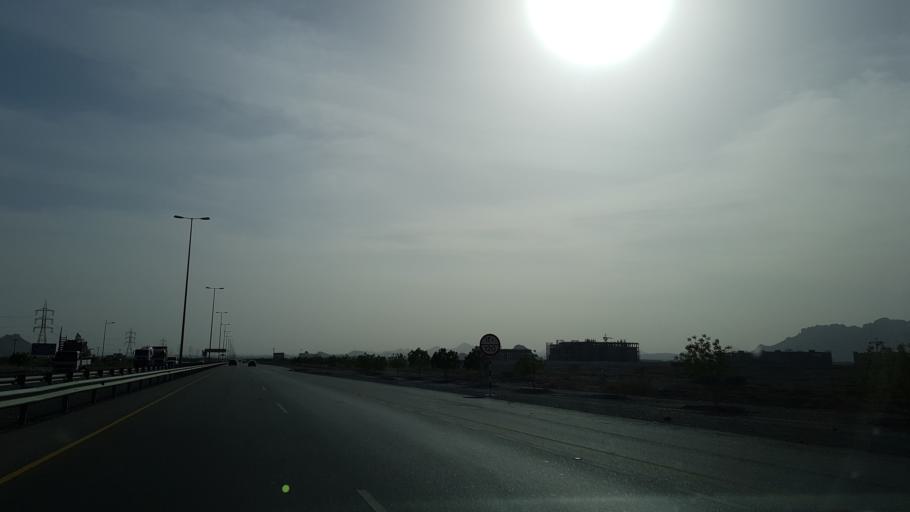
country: OM
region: Muhafazat ad Dakhiliyah
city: Nizwa
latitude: 22.8737
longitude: 57.6141
